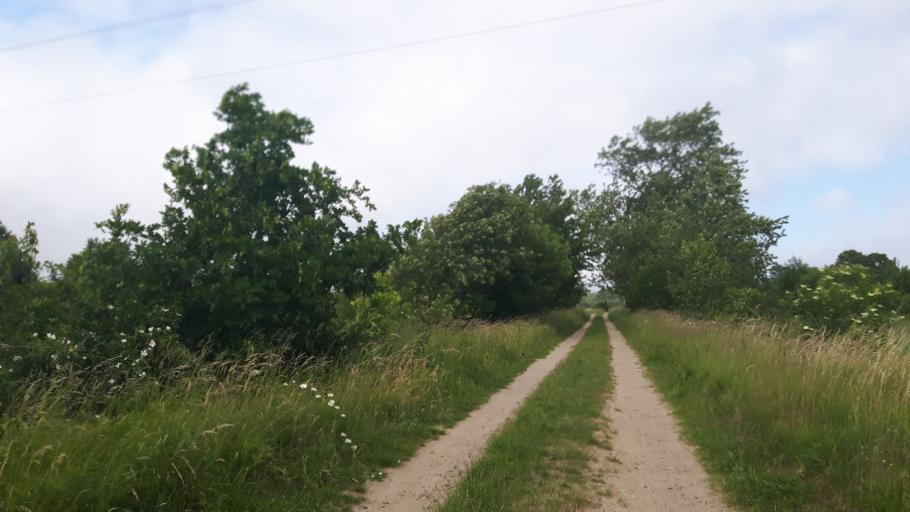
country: PL
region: Pomeranian Voivodeship
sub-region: Slupsk
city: Slupsk
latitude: 54.5989
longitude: 17.0011
